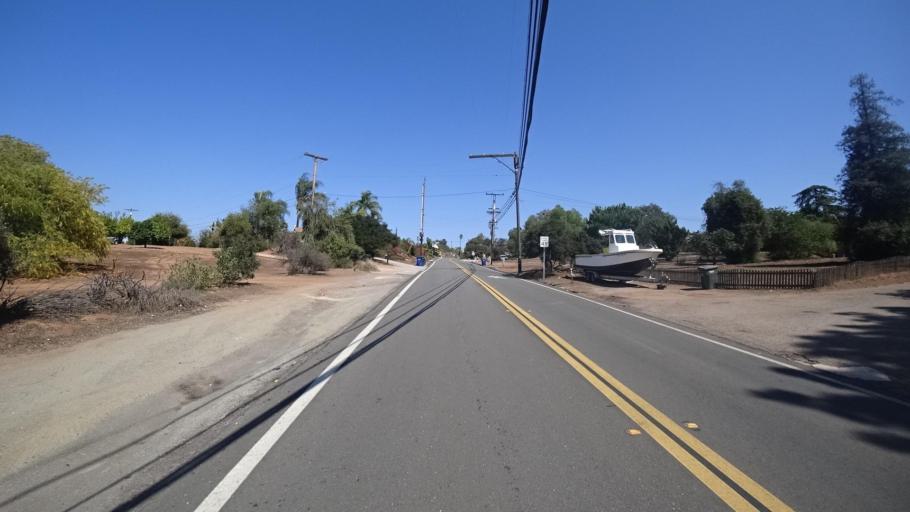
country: US
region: California
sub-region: San Diego County
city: Crest
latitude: 32.8177
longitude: -116.8576
